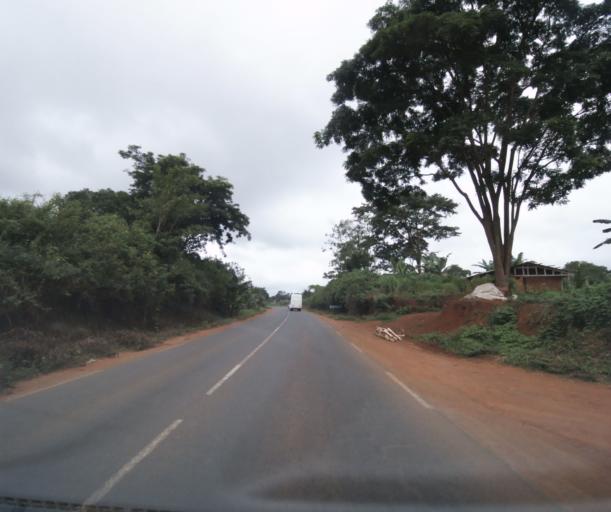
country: CM
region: Centre
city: Mbankomo
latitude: 3.7898
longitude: 11.4359
